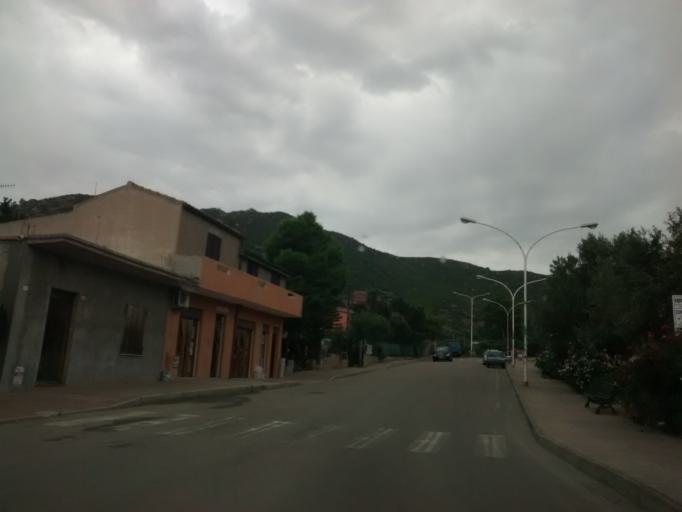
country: IT
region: Sardinia
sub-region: Provincia di Cagliari
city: Villasimius
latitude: 39.1396
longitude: 9.4291
